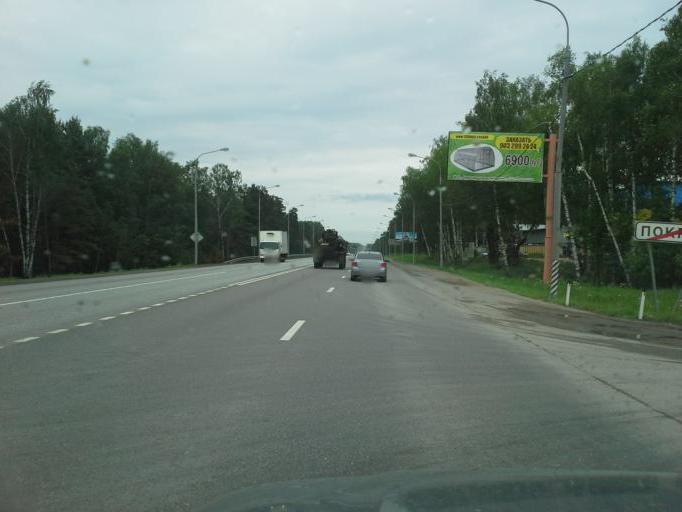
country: RU
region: Vladimir
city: Pokrov
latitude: 55.9205
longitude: 39.2096
